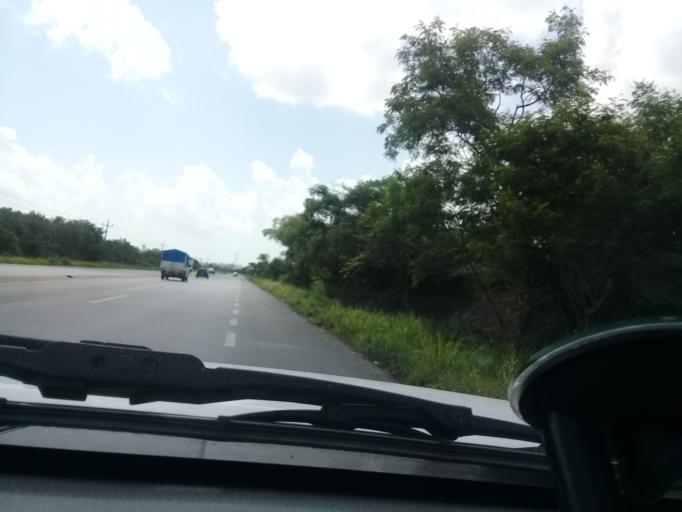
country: MX
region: Veracruz
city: Moralillo
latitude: 22.2125
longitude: -97.9680
